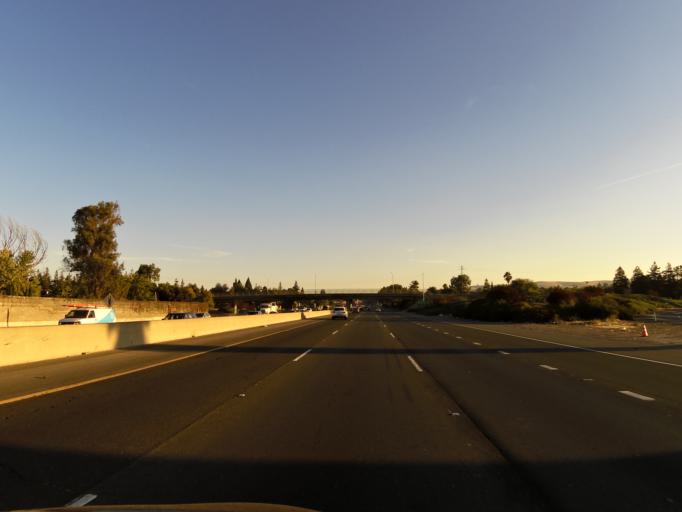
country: US
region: California
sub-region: Contra Costa County
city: Concord
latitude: 37.9955
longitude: -122.0389
